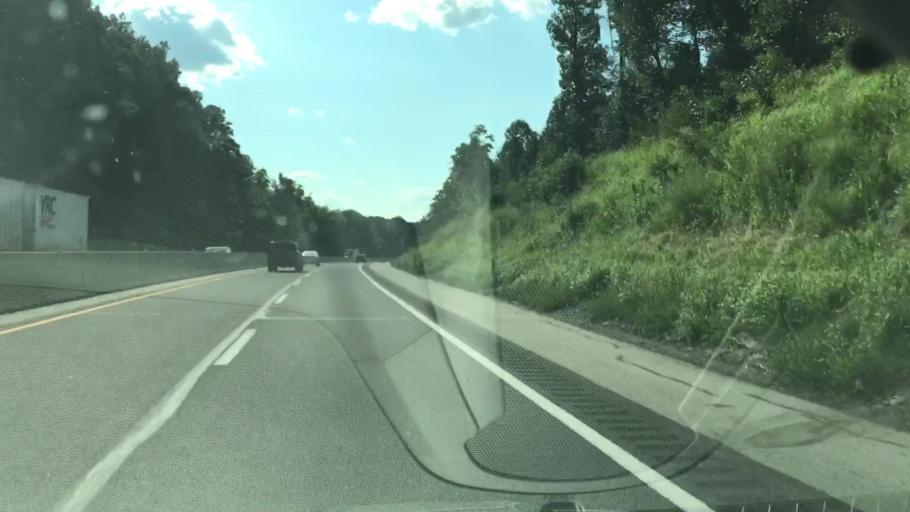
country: US
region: Pennsylvania
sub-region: Lebanon County
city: Cornwall
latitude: 40.2265
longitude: -76.4795
